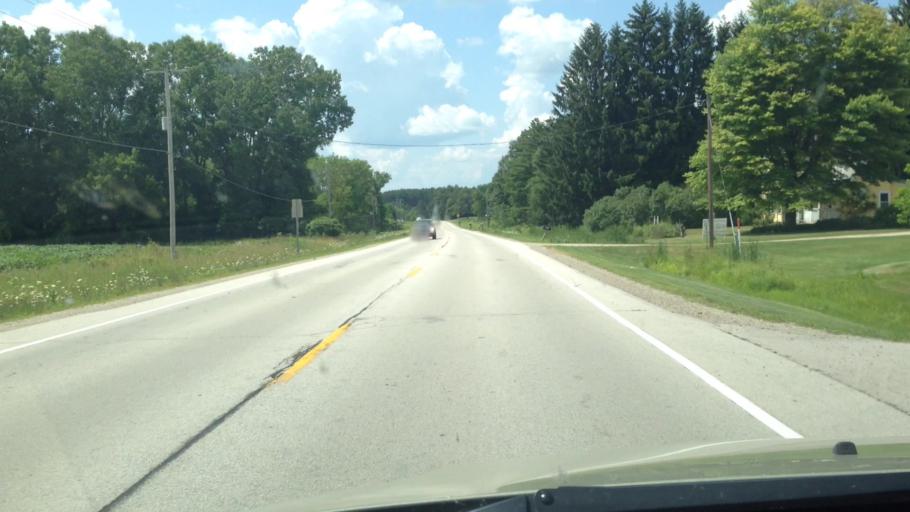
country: US
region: Wisconsin
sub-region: Brown County
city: Suamico
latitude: 44.6450
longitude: -88.0931
